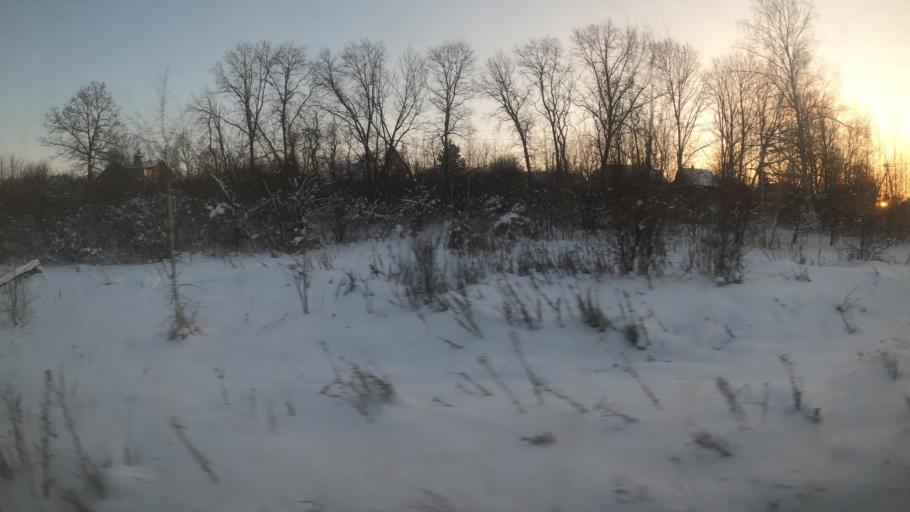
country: RU
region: Moskovskaya
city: Dedenevo
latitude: 56.2525
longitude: 37.5052
